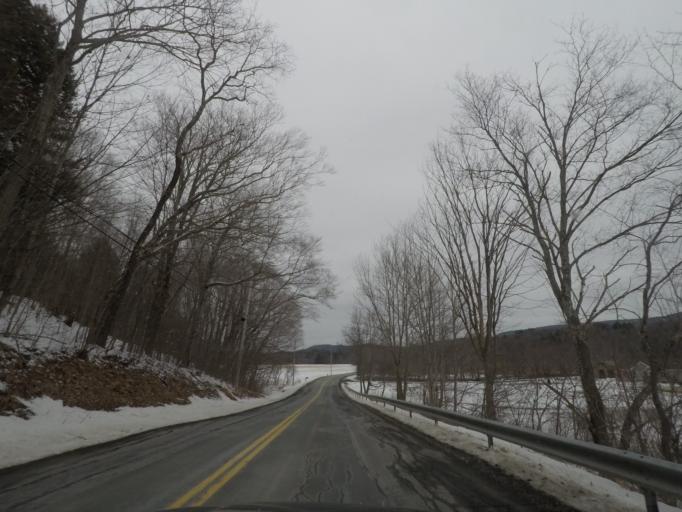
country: US
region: Massachusetts
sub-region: Berkshire County
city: Lanesborough
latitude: 42.5823
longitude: -73.3747
